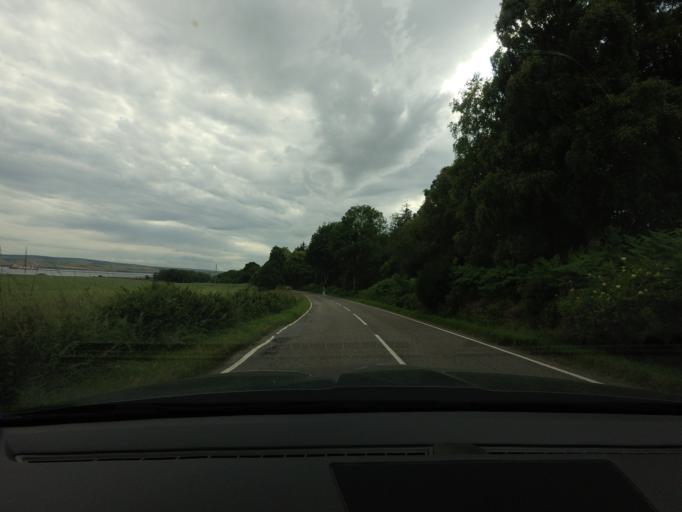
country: GB
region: Scotland
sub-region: Highland
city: Alness
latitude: 57.6941
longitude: -4.2929
